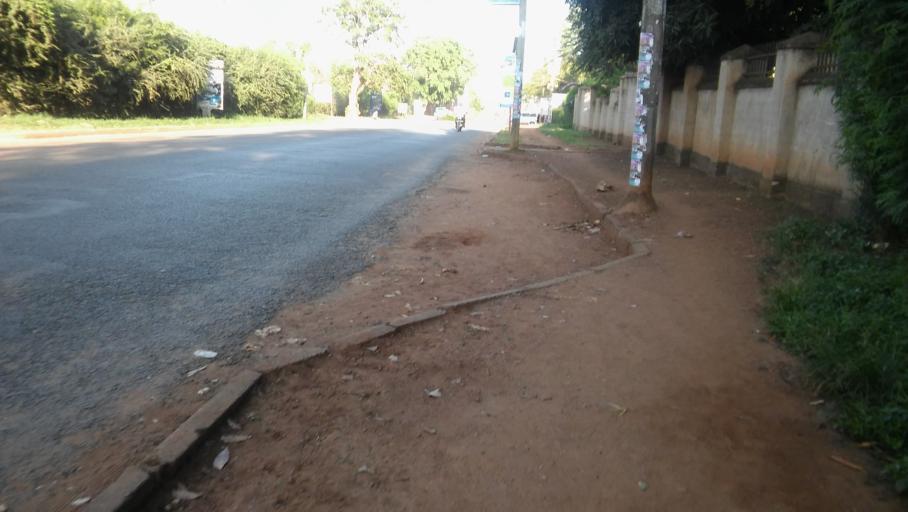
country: UG
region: Eastern Region
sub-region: Mbale District
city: Mbale
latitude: 1.0693
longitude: 34.1852
